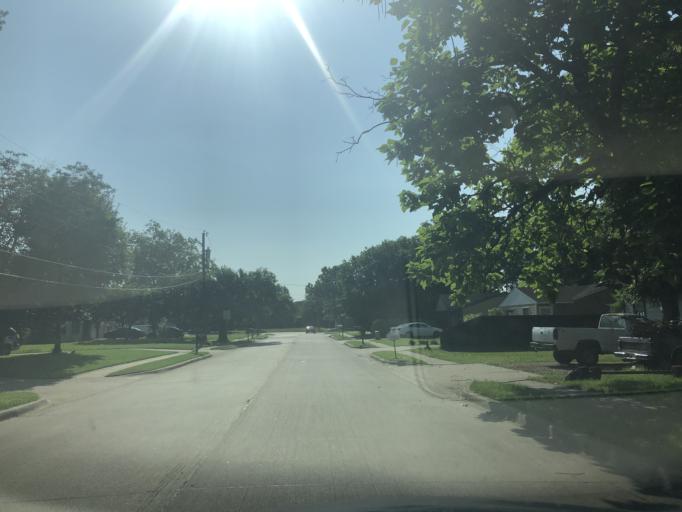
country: US
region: Texas
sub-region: Dallas County
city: Irving
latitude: 32.8106
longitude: -96.9779
